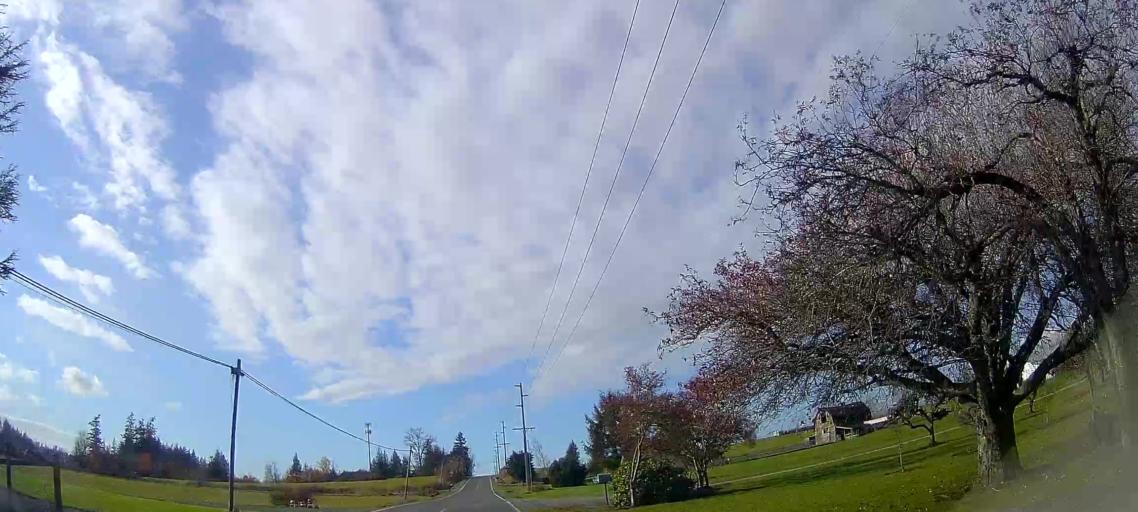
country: US
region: Washington
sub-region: Skagit County
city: Clear Lake
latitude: 48.4352
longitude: -122.2512
